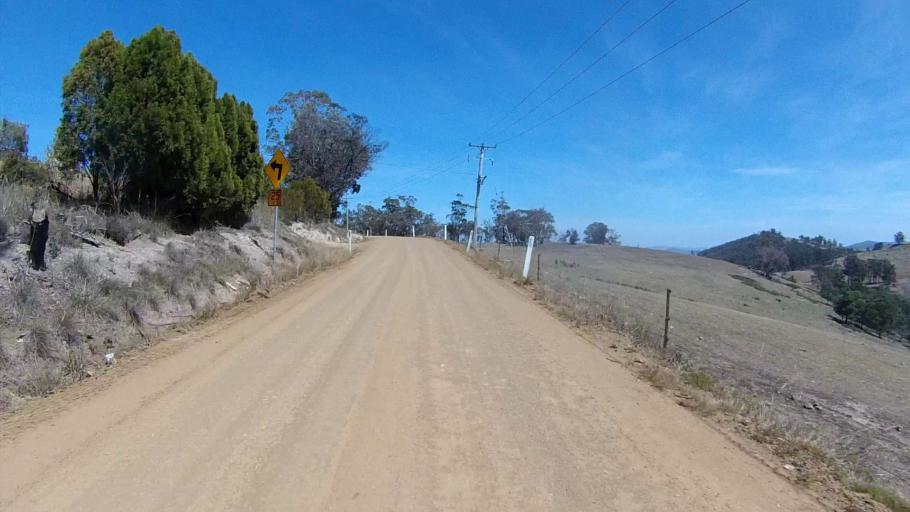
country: AU
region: Tasmania
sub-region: Sorell
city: Sorell
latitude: -42.7810
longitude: 147.6460
